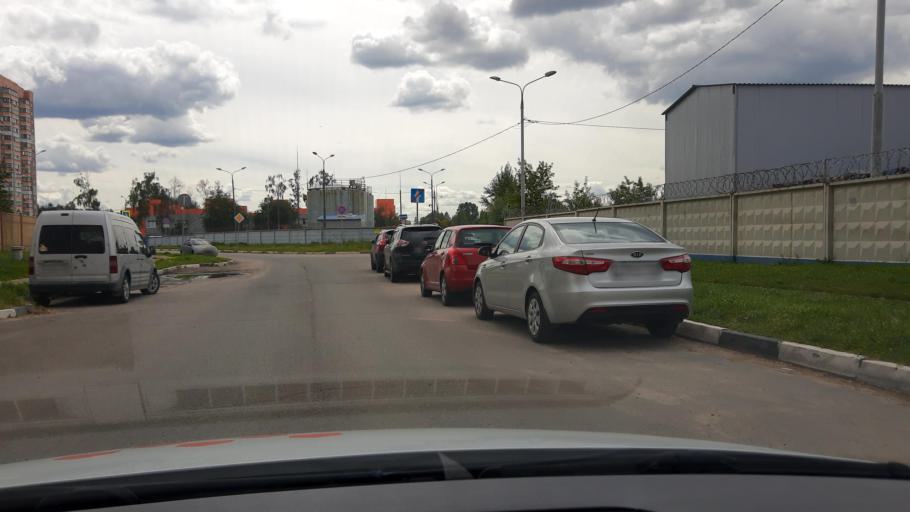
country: RU
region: Moskovskaya
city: Zheleznodorozhnyy
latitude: 55.7423
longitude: 37.9816
